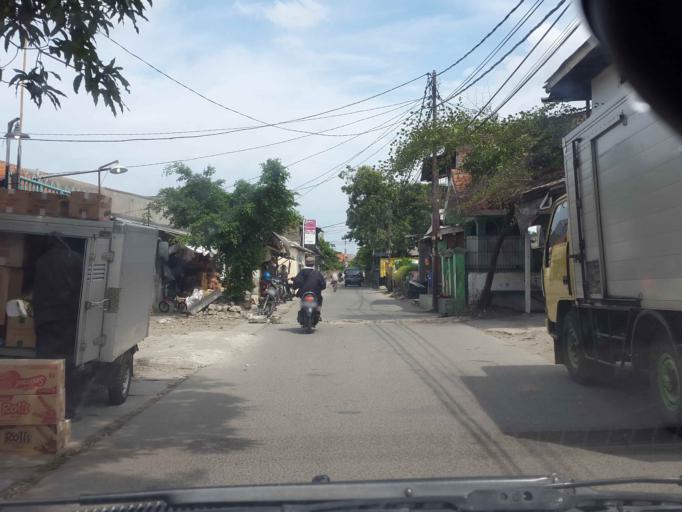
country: ID
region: Banten
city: Tangerang
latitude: -6.1498
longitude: 106.6775
